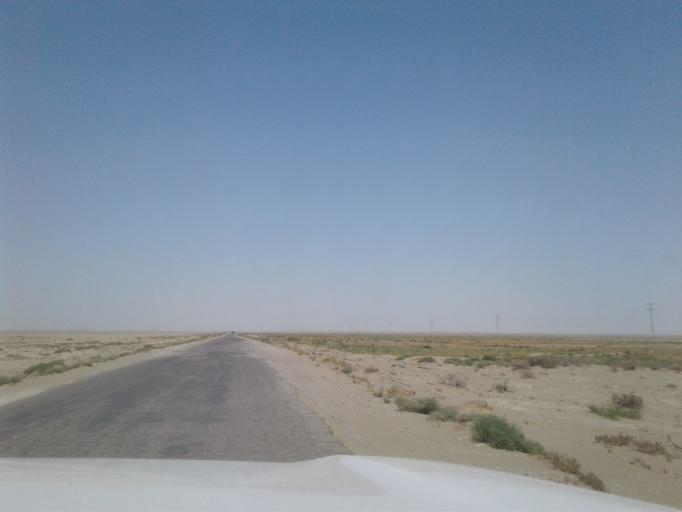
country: TM
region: Balkan
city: Gumdag
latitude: 38.3307
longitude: 54.3536
